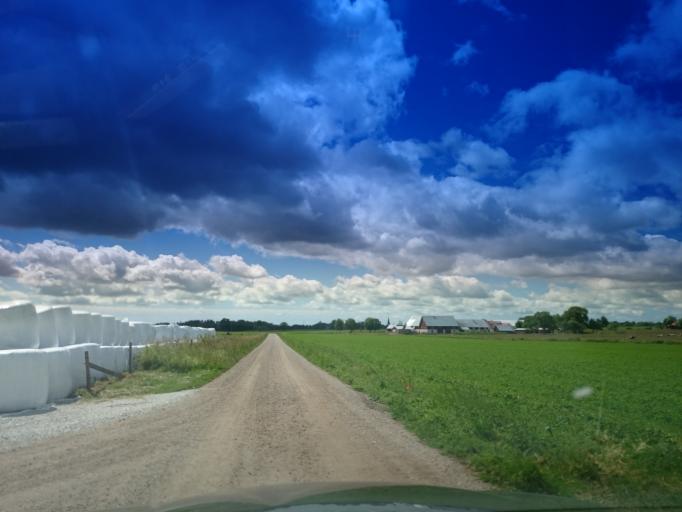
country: SE
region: Gotland
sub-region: Gotland
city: Hemse
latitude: 57.3450
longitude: 18.6406
